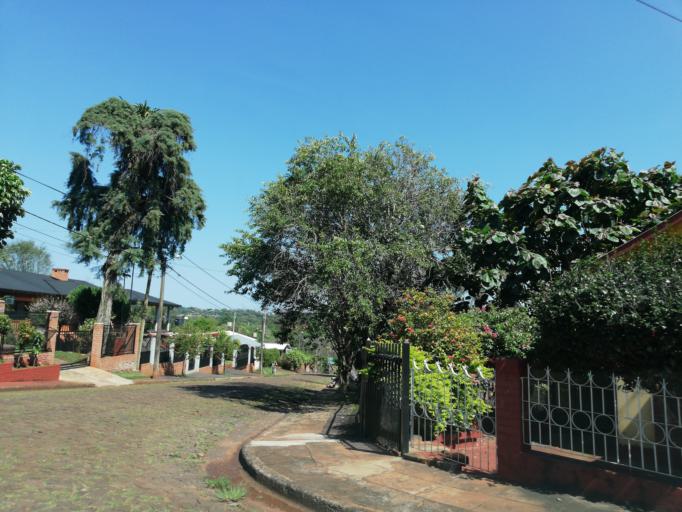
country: AR
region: Misiones
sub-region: Departamento de Eldorado
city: Eldorado
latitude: -26.4085
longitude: -54.6135
